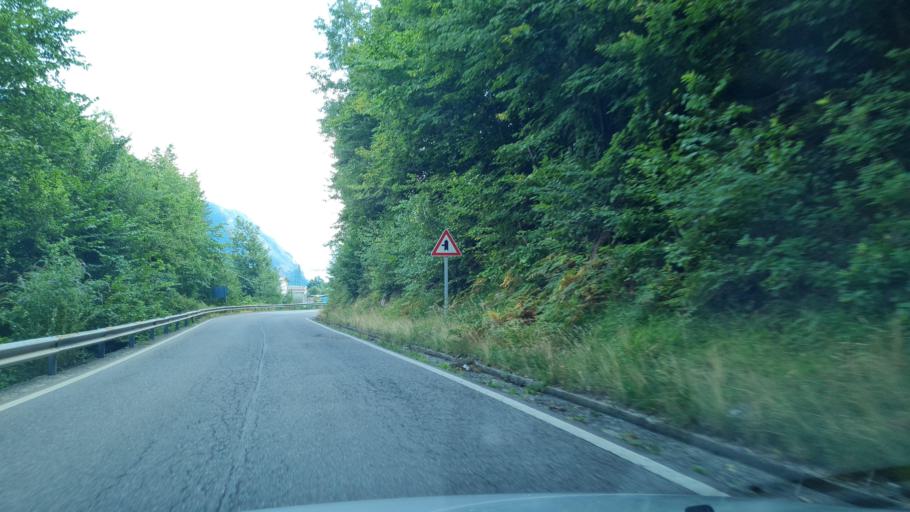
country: IT
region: Piedmont
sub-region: Provincia Verbano-Cusio-Ossola
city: Baceno
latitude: 46.2499
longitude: 8.3235
